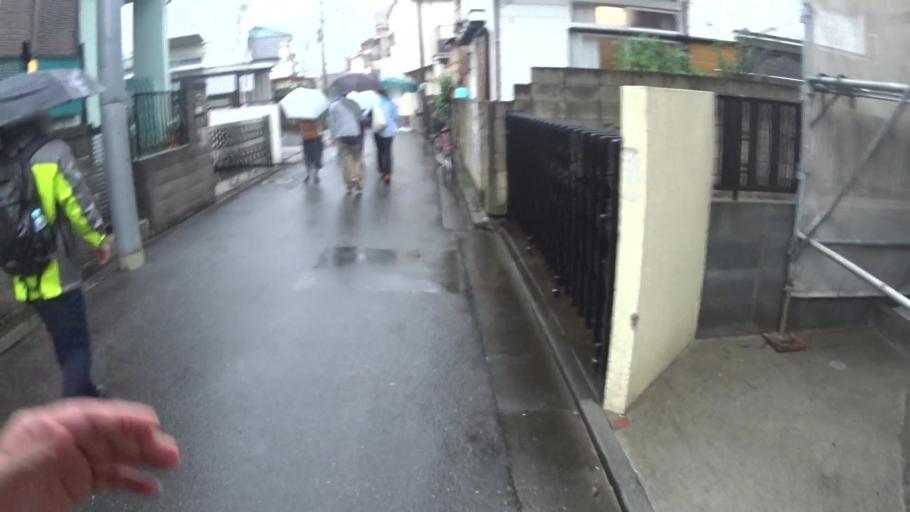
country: JP
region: Saitama
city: Wako
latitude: 35.7453
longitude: 139.6625
